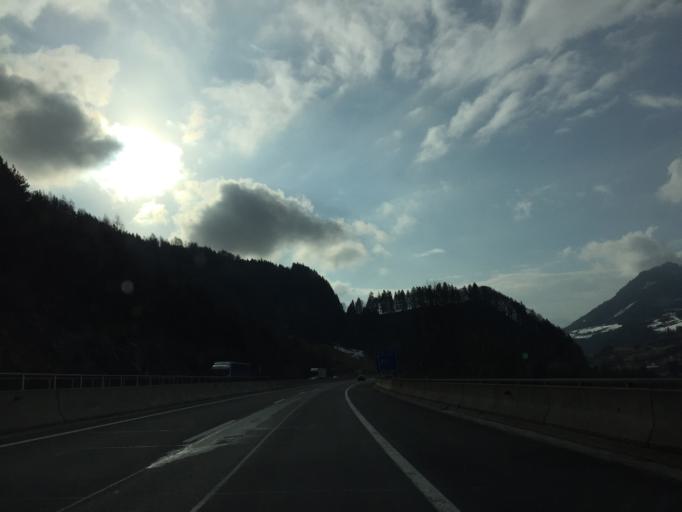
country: AT
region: Salzburg
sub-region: Politischer Bezirk Sankt Johann im Pongau
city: Werfen
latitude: 47.4850
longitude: 13.1928
